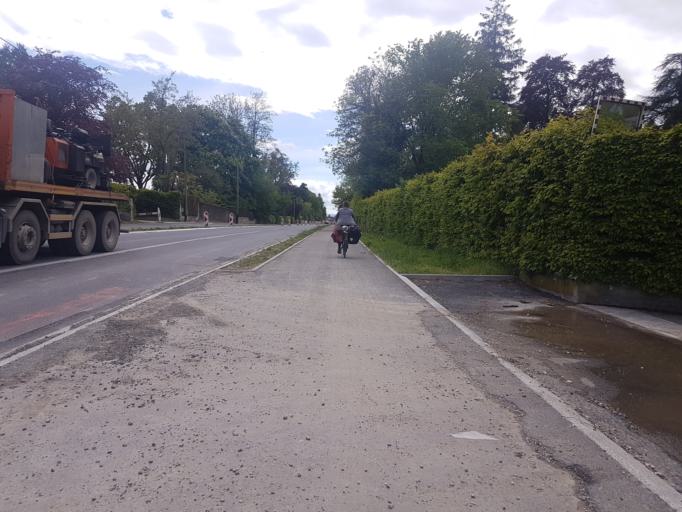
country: CH
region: Vaud
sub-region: Nyon District
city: Coppet
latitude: 46.3238
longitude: 6.1977
